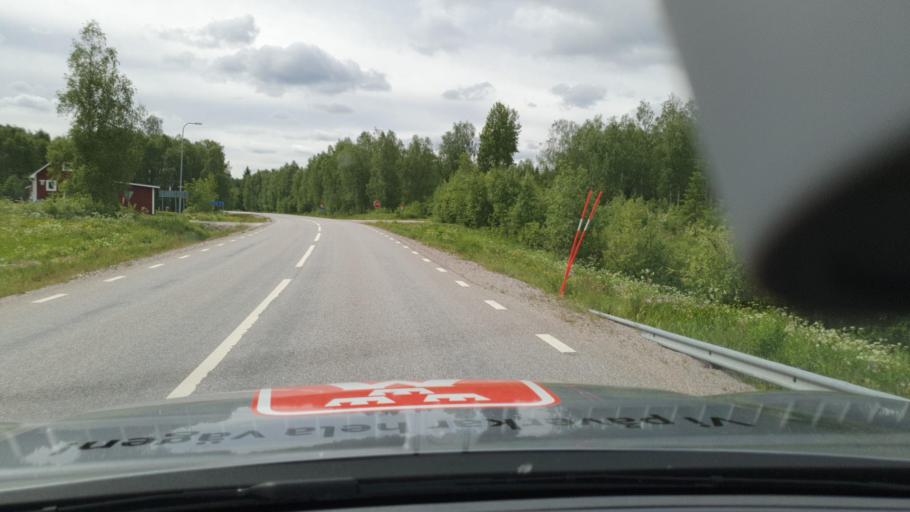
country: SE
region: Norrbotten
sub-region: Kalix Kommun
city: Kalix
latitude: 65.9812
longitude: 23.4619
